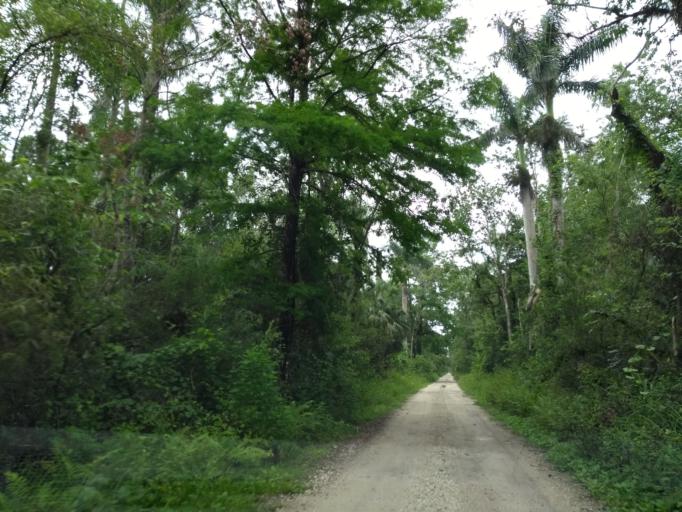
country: US
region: Florida
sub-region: Collier County
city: Lely Resort
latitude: 26.0045
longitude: -81.4112
